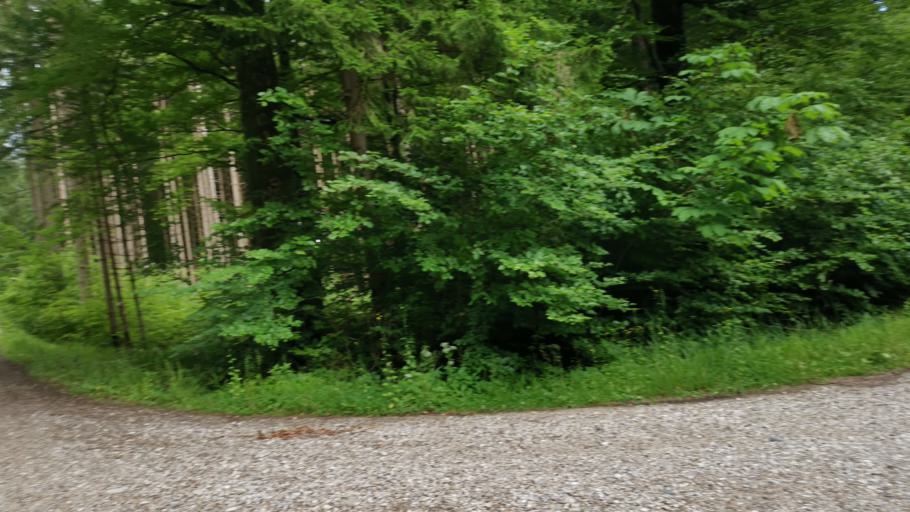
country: DE
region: Bavaria
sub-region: Upper Bavaria
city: Schaftlarn
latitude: 48.0078
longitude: 11.4472
